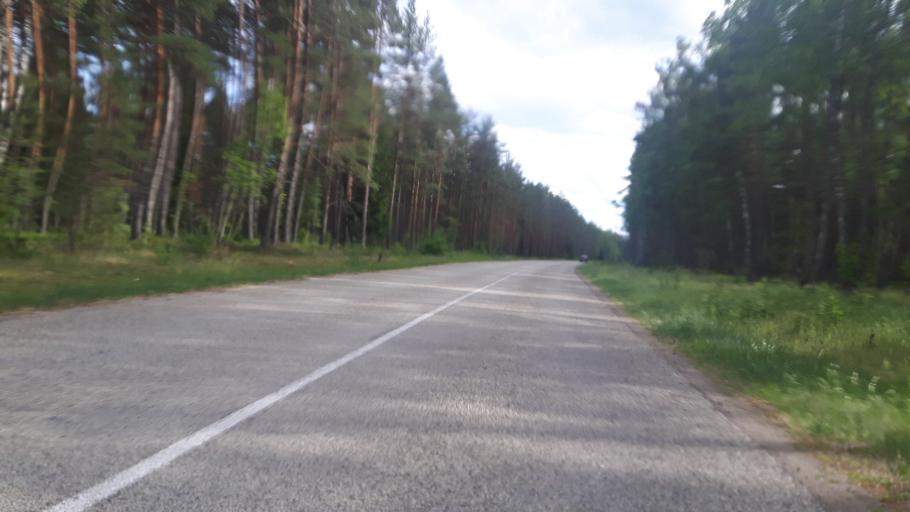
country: LV
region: Engure
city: Smarde
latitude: 57.0210
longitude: 23.3455
